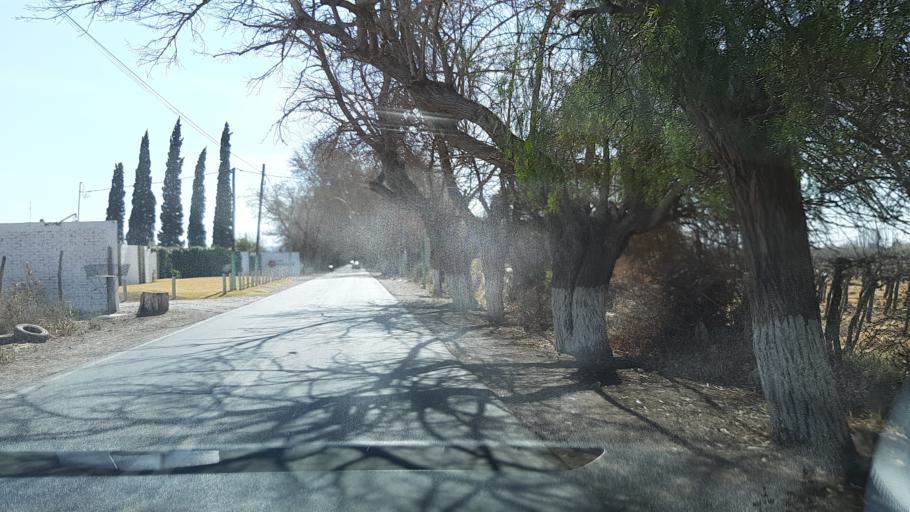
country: AR
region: San Juan
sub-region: Departamento de Rivadavia
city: Rivadavia
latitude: -31.5316
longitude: -68.6185
